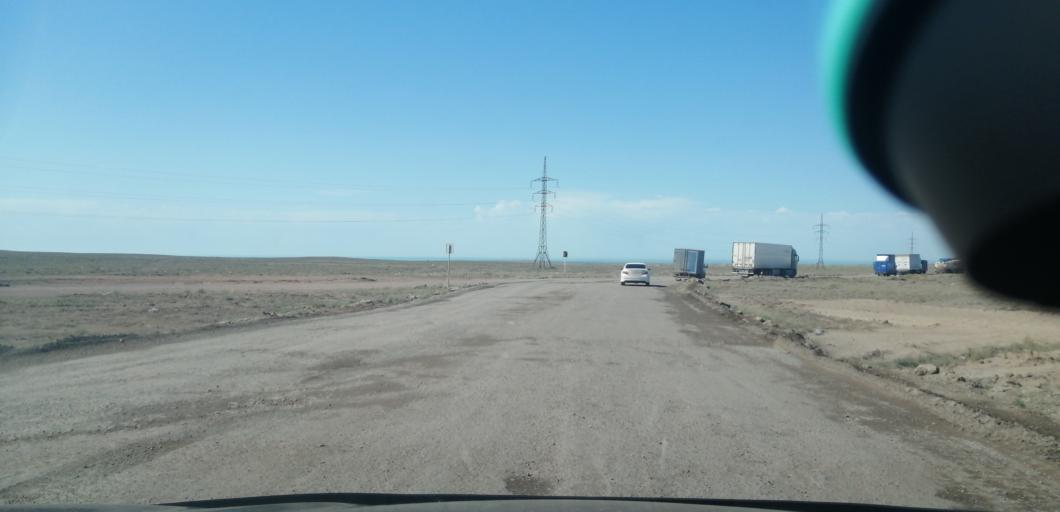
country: KZ
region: Qaraghandy
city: Balqash
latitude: 46.8245
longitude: 74.7755
